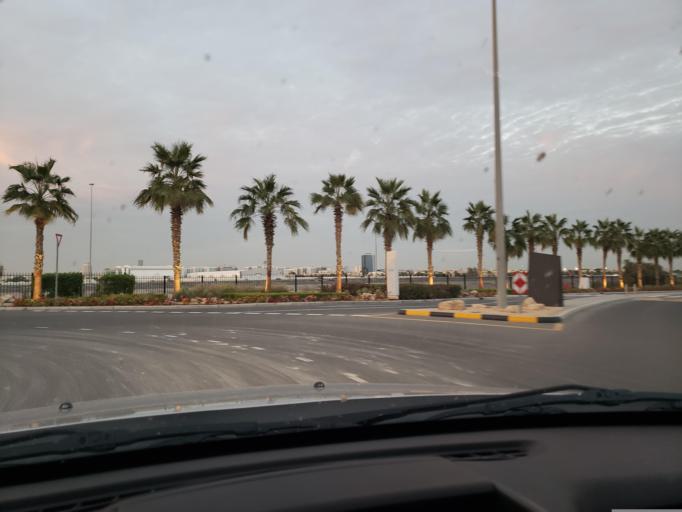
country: AE
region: Dubai
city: Dubai
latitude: 25.0270
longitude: 55.2477
